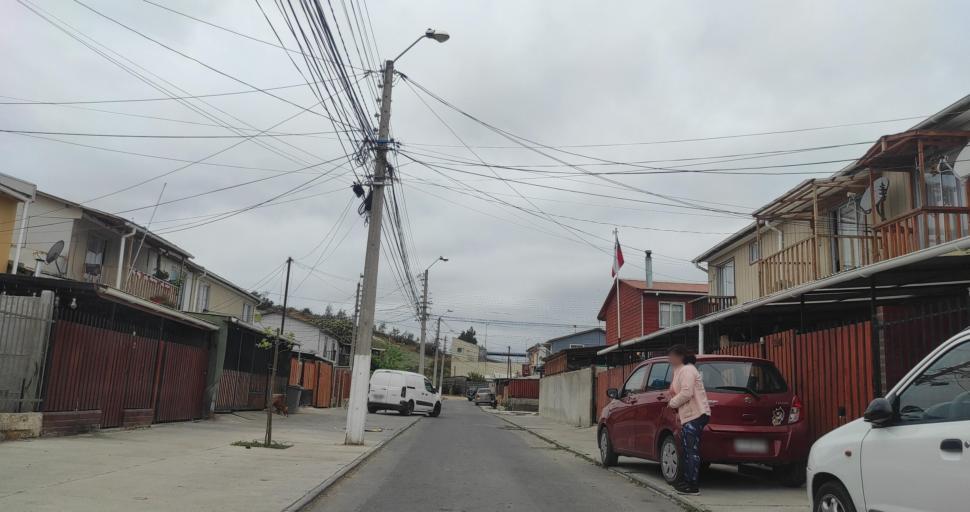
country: CL
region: Valparaiso
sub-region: Provincia de Marga Marga
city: Limache
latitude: -33.0190
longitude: -71.2638
